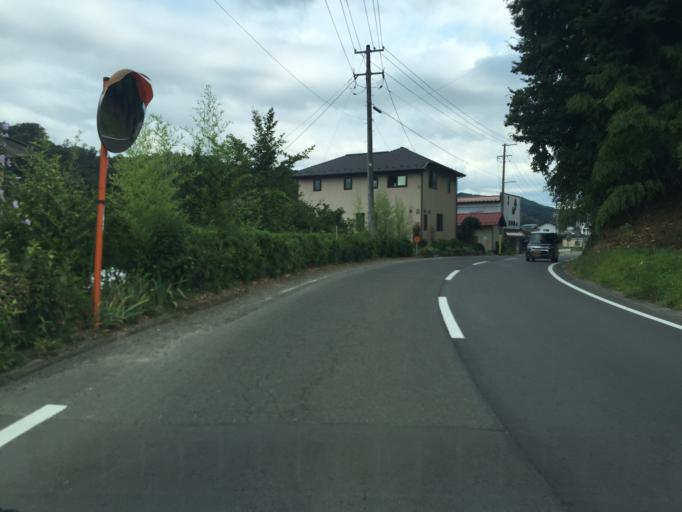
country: JP
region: Fukushima
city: Hobaramachi
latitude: 37.7282
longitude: 140.5996
